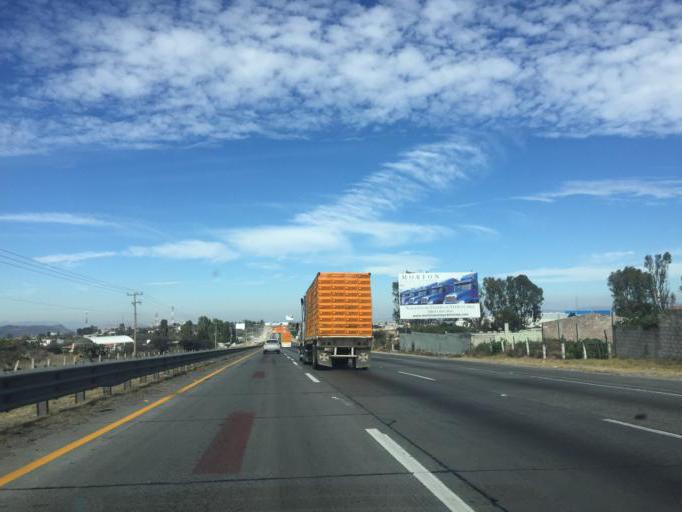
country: MX
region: Queretaro
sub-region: San Juan del Rio
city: Paso de Mata
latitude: 20.3481
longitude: -99.9502
